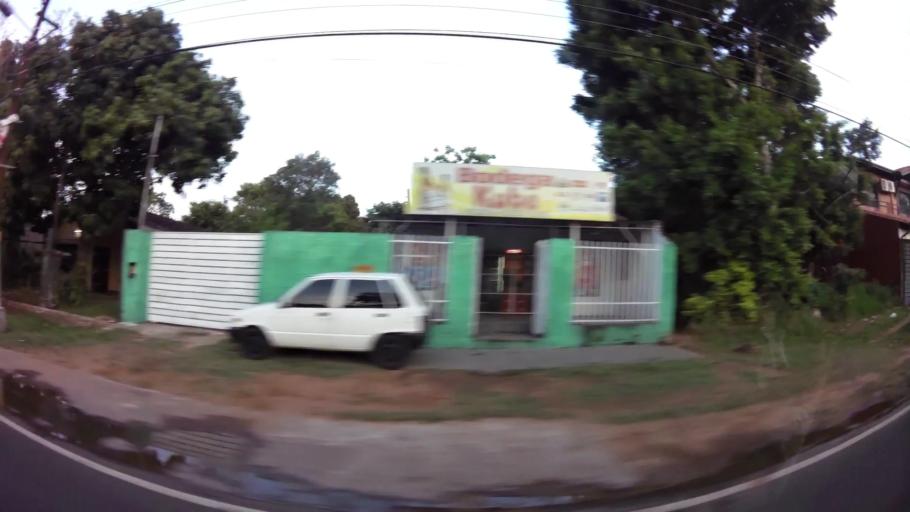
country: PY
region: Central
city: San Lorenzo
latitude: -25.3549
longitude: -57.4908
